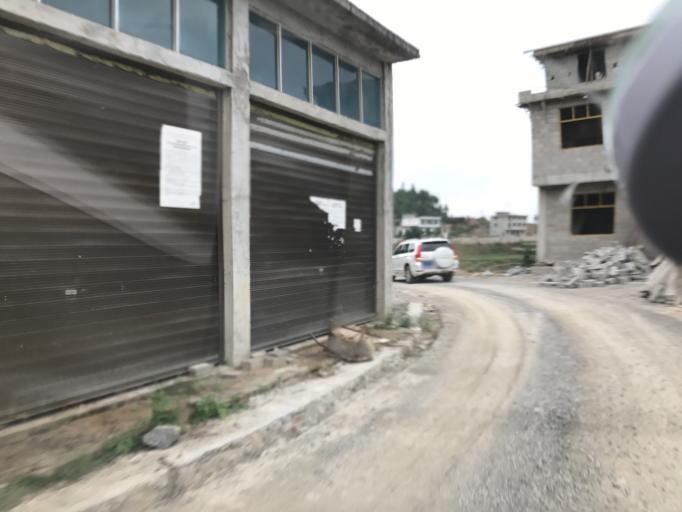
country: CN
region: Guizhou Sheng
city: Donghua
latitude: 28.0553
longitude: 108.1080
